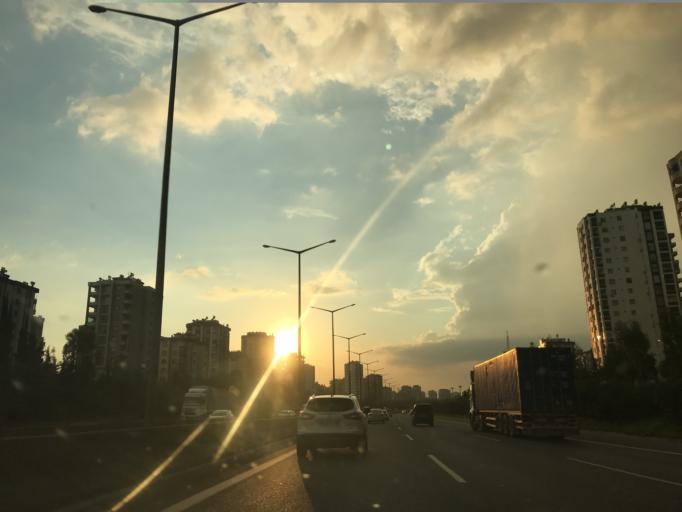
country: TR
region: Adana
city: Seyhan
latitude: 37.0308
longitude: 35.2805
